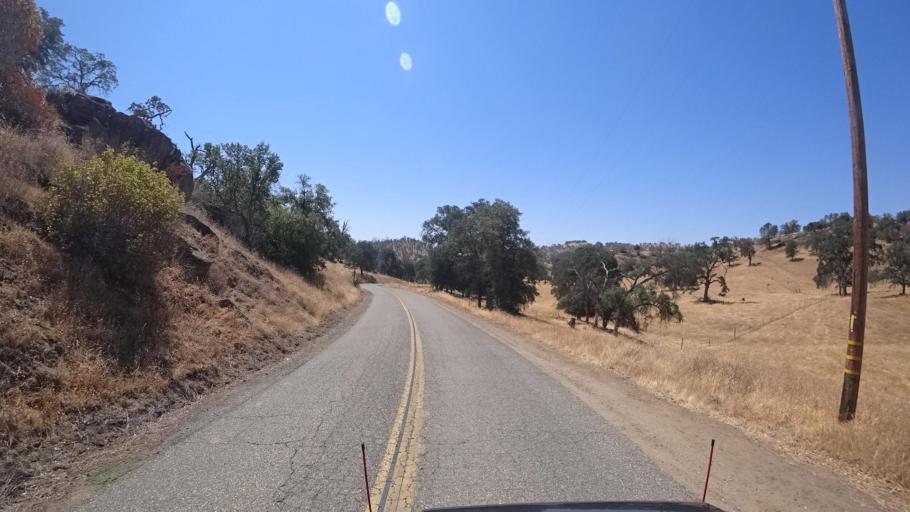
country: US
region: California
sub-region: Mariposa County
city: Mariposa
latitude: 37.2888
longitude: -119.9771
